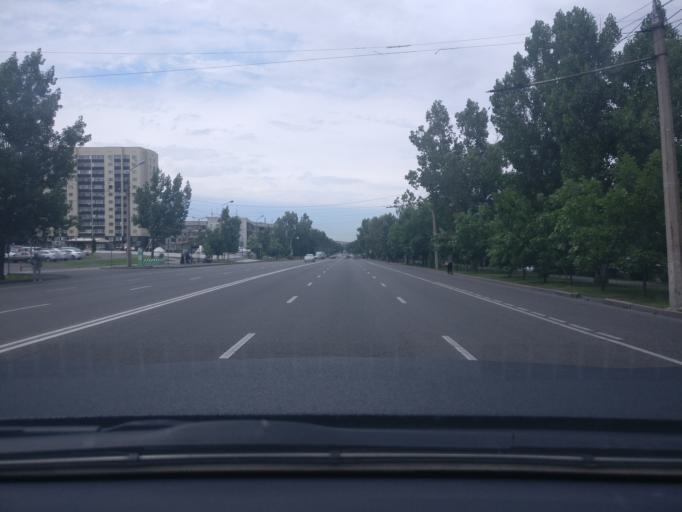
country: KZ
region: Almaty Qalasy
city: Almaty
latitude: 43.2393
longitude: 76.8593
